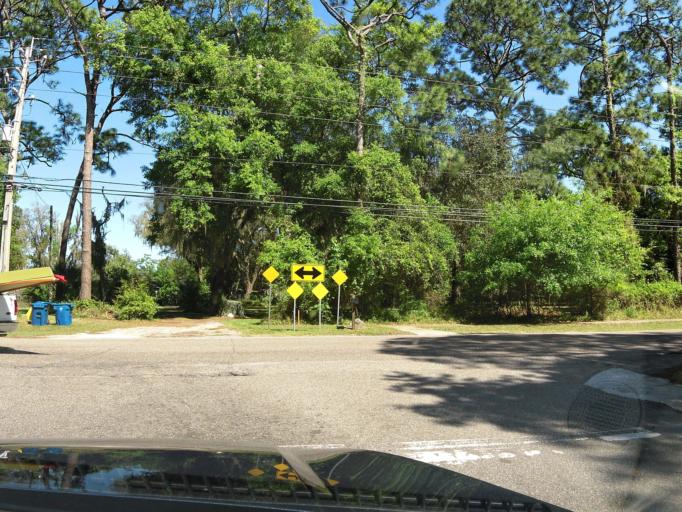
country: US
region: Florida
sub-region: Duval County
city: Jacksonville
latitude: 30.4510
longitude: -81.6015
